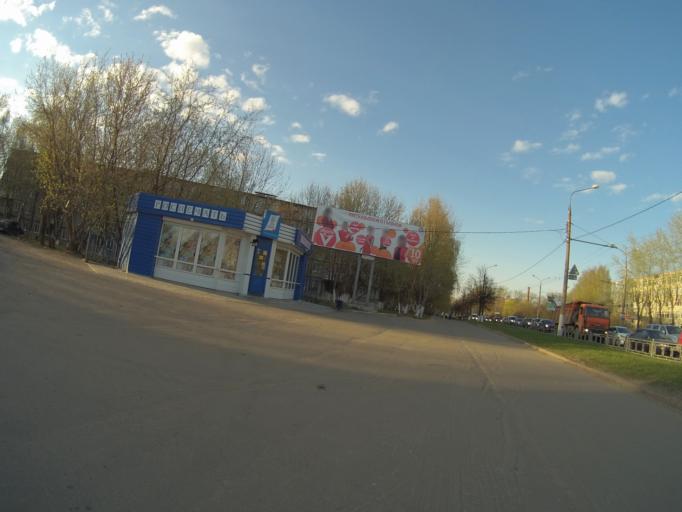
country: RU
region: Vladimir
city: Vladimir
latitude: 56.1451
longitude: 40.3696
